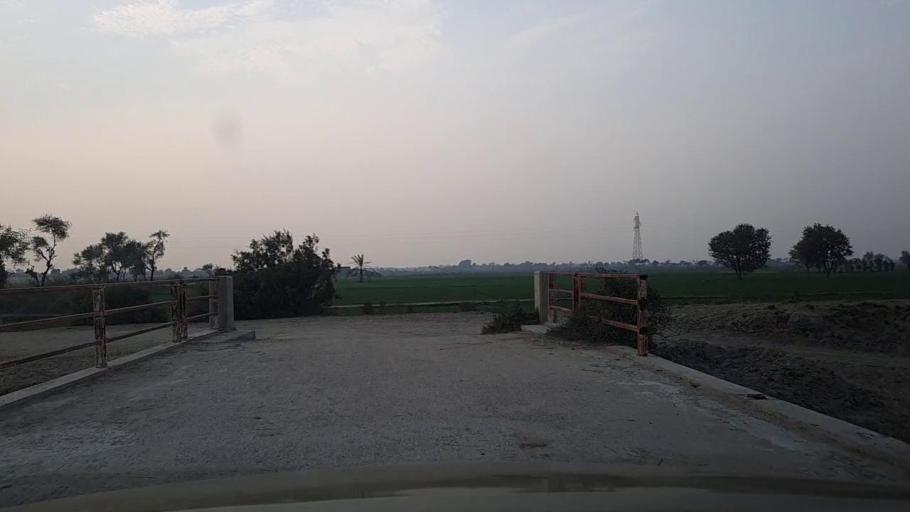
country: PK
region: Sindh
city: Sanghar
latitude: 26.1859
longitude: 68.9538
